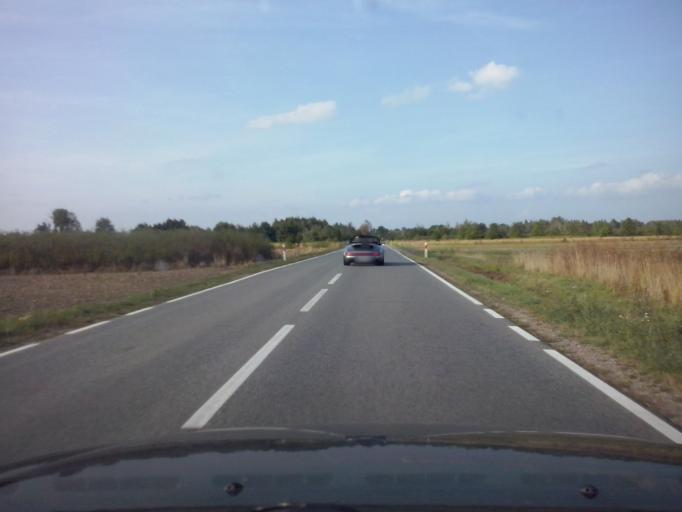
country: PL
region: Subcarpathian Voivodeship
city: Nowa Sarzyna
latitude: 50.3593
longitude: 22.3205
